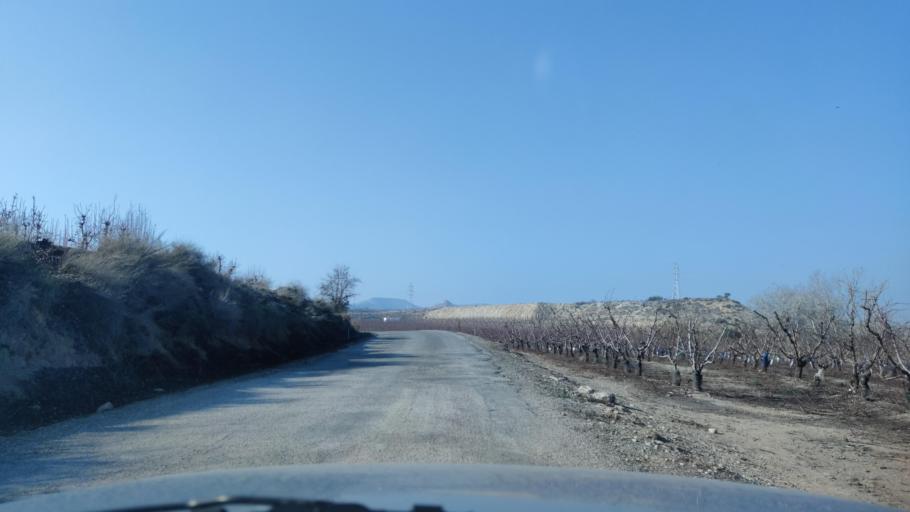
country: ES
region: Catalonia
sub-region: Provincia de Lleida
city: Seros
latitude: 41.4659
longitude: 0.3908
